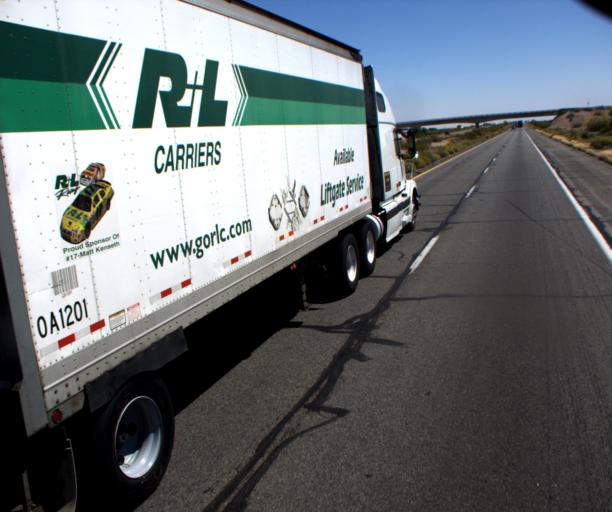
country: US
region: Arizona
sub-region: Maricopa County
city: Buckeye
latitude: 33.4824
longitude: -112.8707
